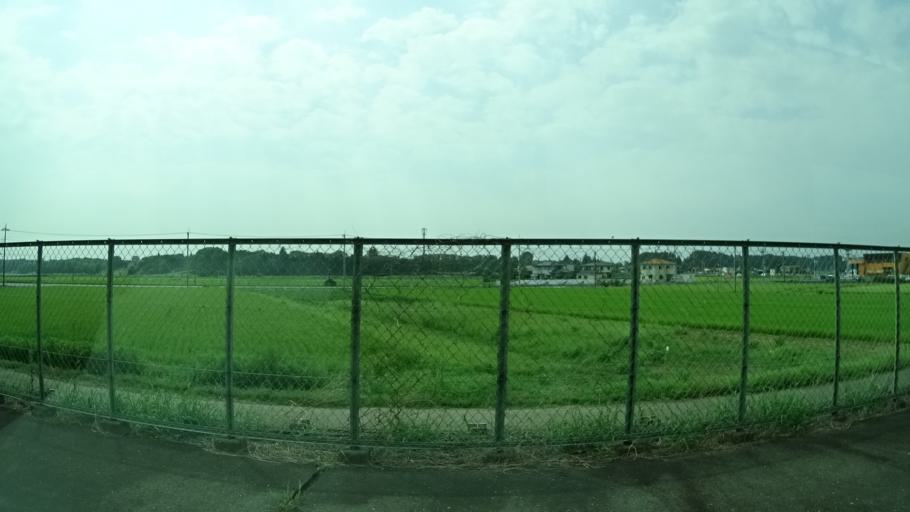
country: JP
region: Tochigi
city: Mashiko
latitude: 36.4919
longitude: 140.0943
